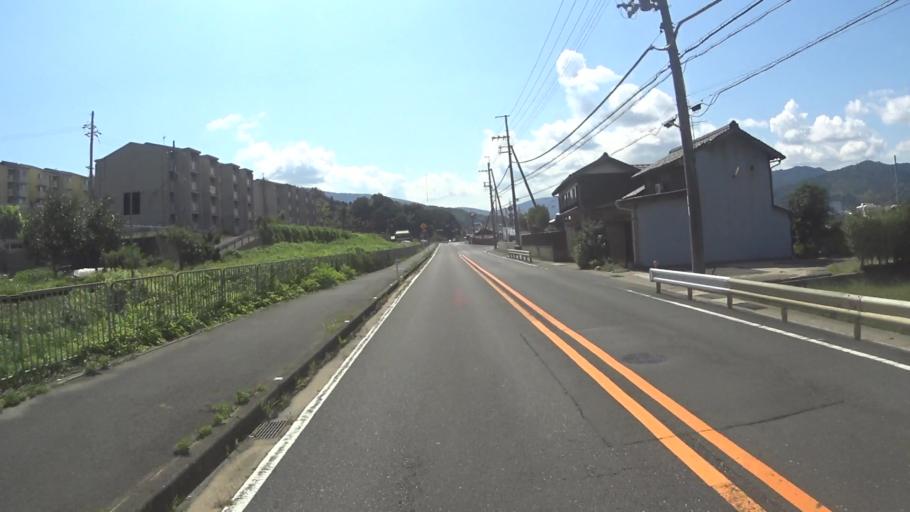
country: JP
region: Kyoto
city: Miyazu
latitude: 35.5437
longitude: 135.2101
